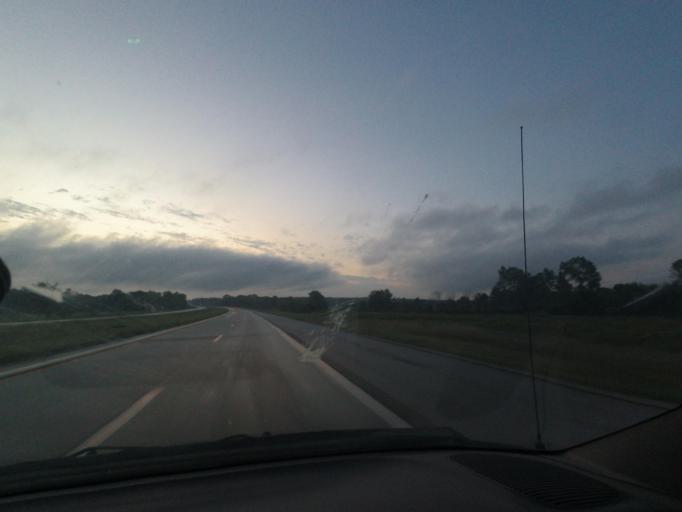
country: US
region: Missouri
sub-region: Linn County
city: Brookfield
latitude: 39.7650
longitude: -93.0447
